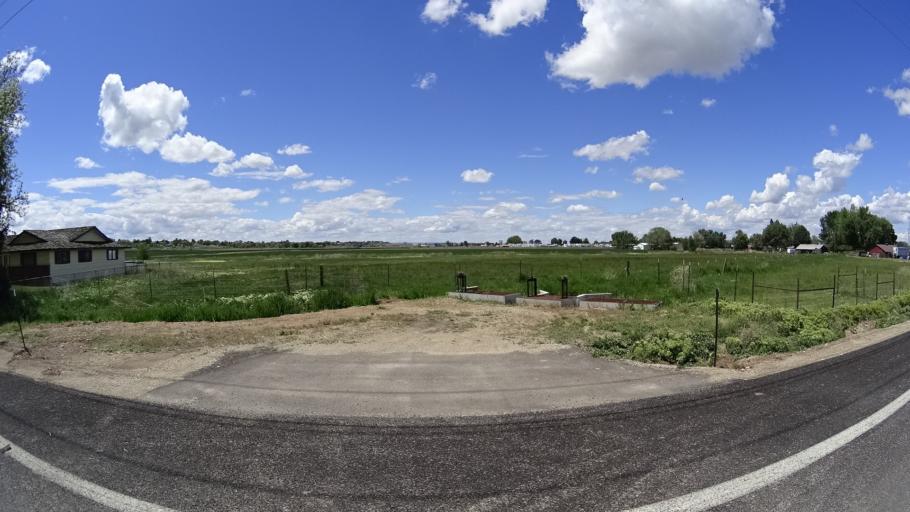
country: US
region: Idaho
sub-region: Ada County
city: Meridian
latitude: 43.6029
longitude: -116.4538
